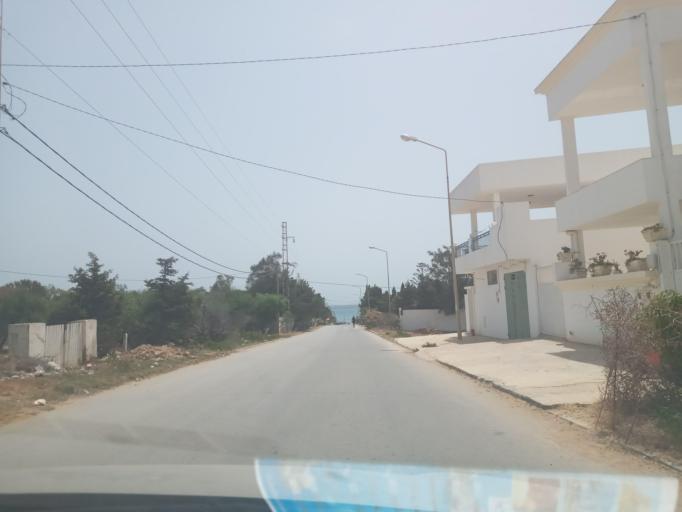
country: TN
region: Nabul
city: El Haouaria
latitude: 37.0364
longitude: 11.0546
